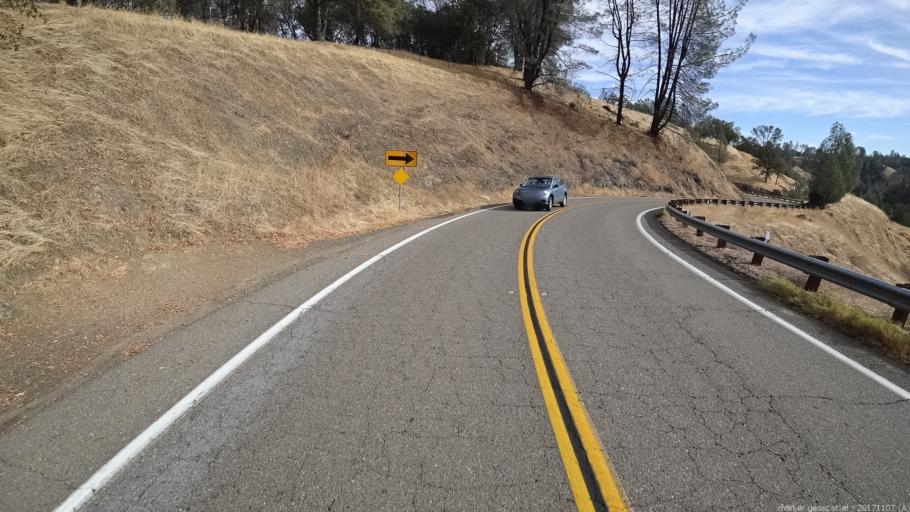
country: US
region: California
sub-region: Shasta County
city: Shasta
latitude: 40.5119
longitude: -122.5217
